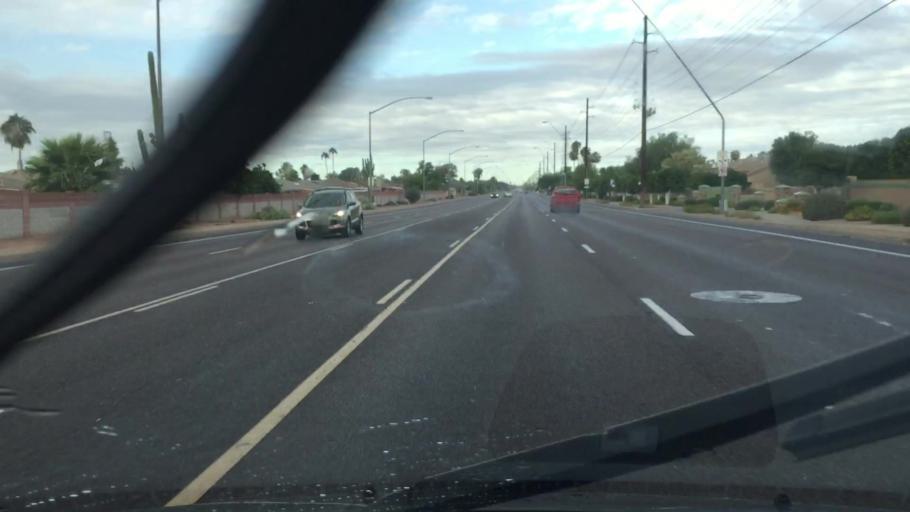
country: US
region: Arizona
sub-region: Maricopa County
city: Gilbert
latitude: 33.4084
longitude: -111.7402
